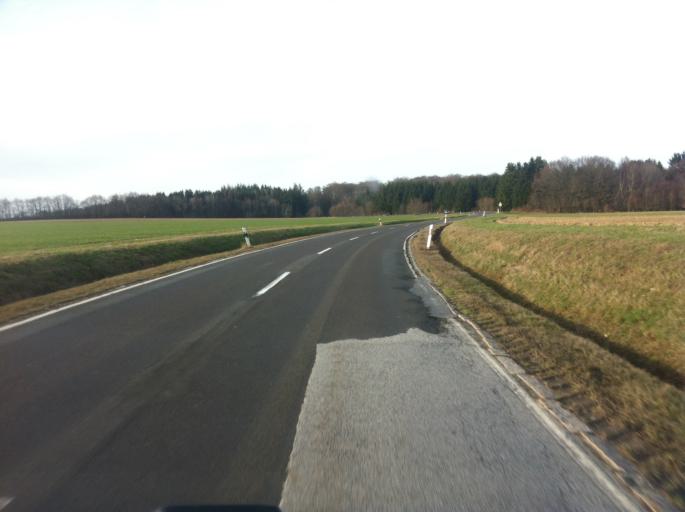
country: DE
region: Rheinland-Pfalz
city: Barenbach
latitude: 49.9547
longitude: 7.2957
